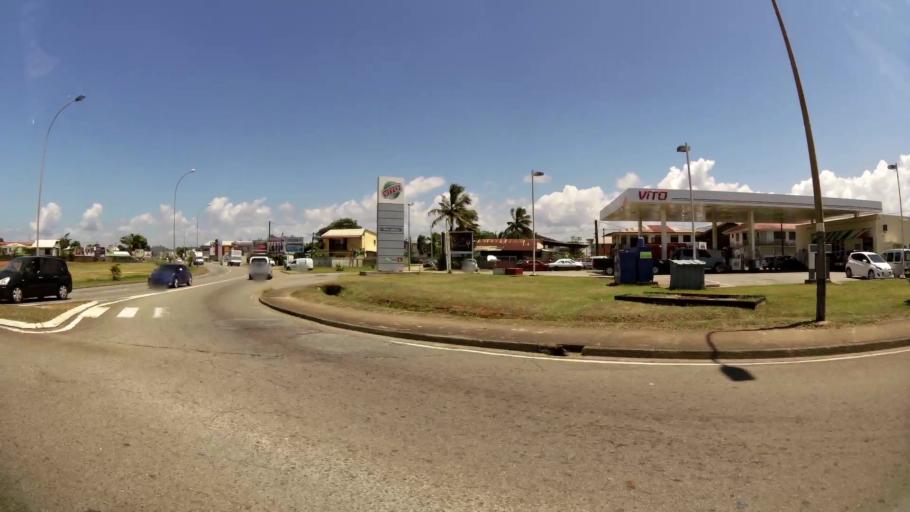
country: GF
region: Guyane
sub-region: Guyane
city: Cayenne
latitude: 4.9322
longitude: -52.3267
